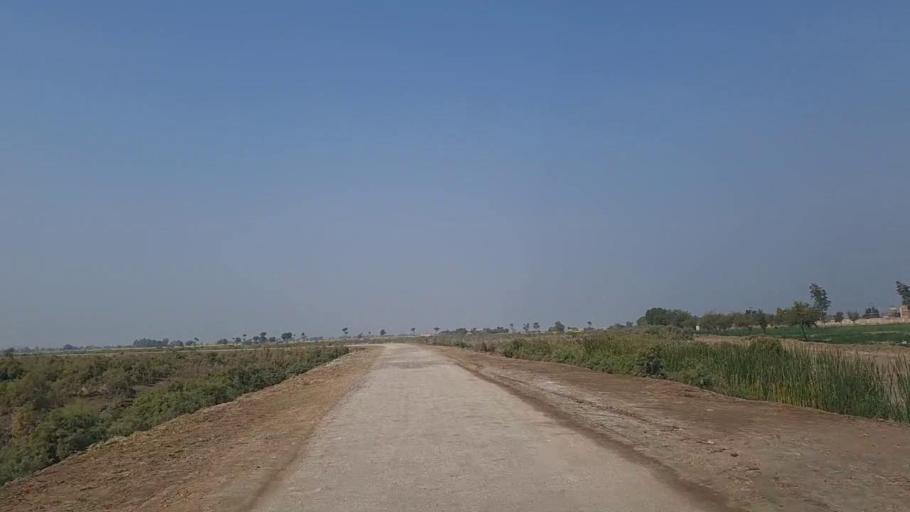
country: PK
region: Sindh
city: Nawabshah
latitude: 26.3592
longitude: 68.4373
